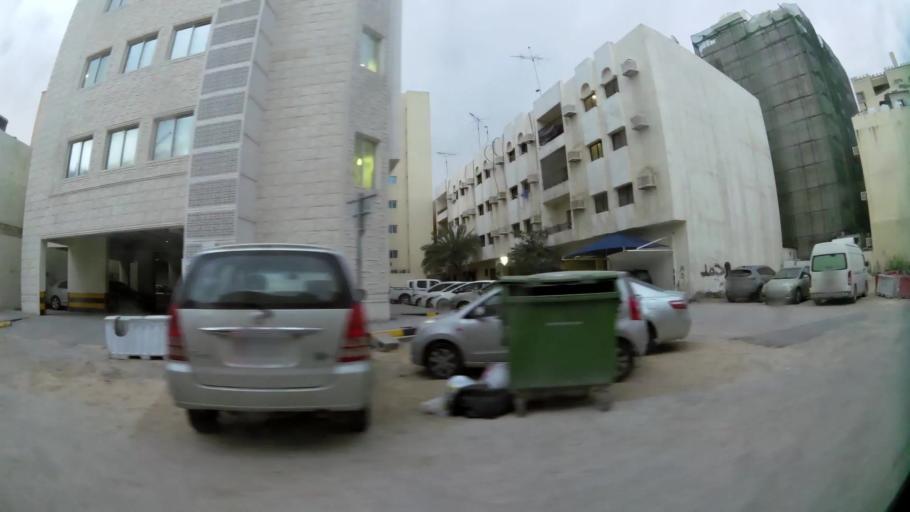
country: QA
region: Baladiyat ad Dawhah
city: Doha
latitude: 25.2732
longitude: 51.5267
